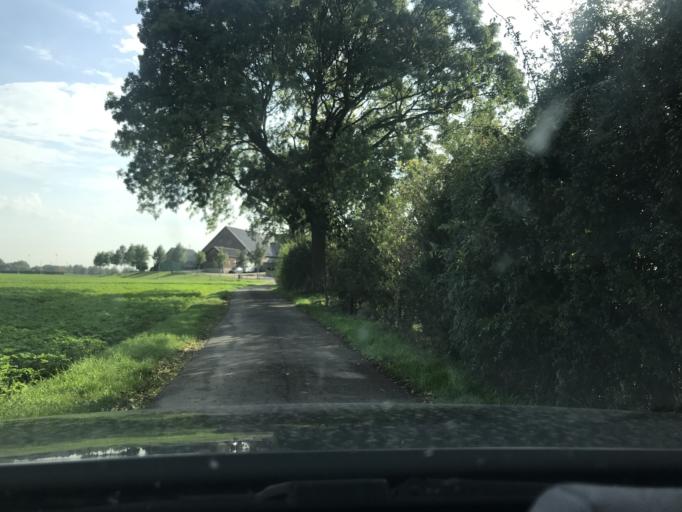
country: DE
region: North Rhine-Westphalia
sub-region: Regierungsbezirk Dusseldorf
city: Kleve
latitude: 51.8161
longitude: 6.1903
